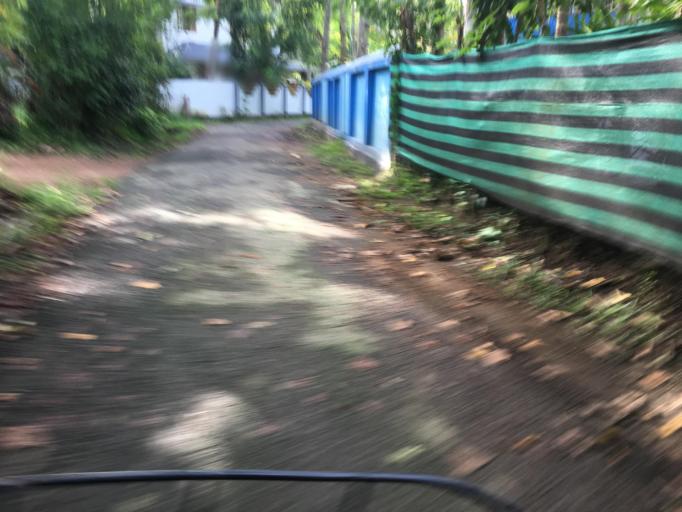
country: IN
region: Kerala
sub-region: Alappuzha
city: Kattanam
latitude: 9.1989
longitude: 76.5355
